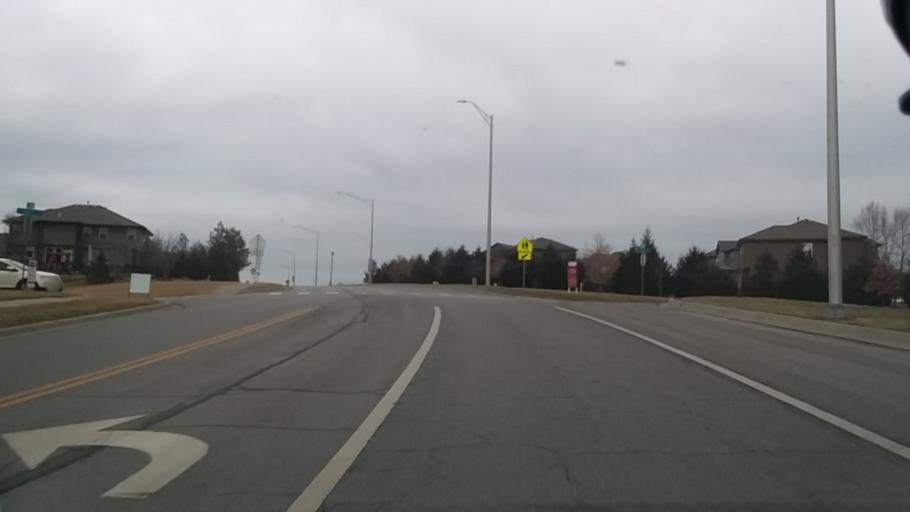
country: US
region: Kansas
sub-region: Johnson County
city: Olathe
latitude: 38.9026
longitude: -94.8634
